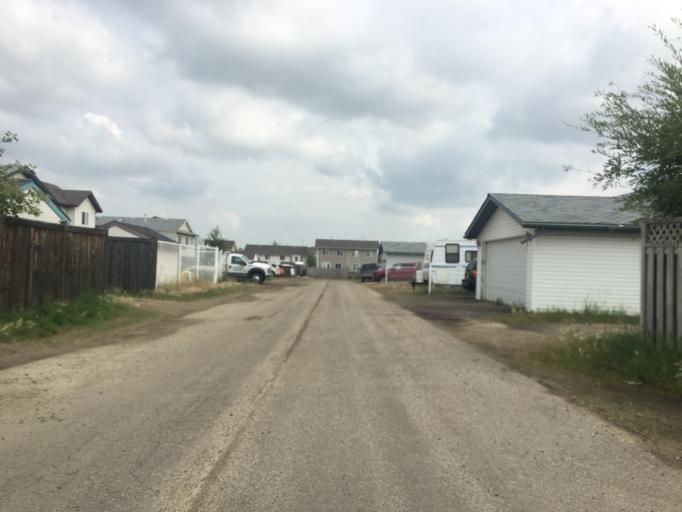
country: CA
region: Alberta
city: Grande Prairie
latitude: 55.1459
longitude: -118.8167
